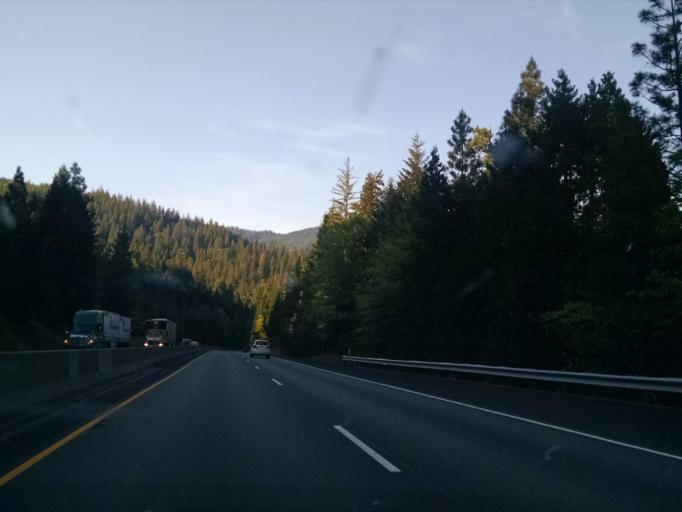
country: US
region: California
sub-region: Siskiyou County
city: Dunsmuir
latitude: 41.0858
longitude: -122.3519
